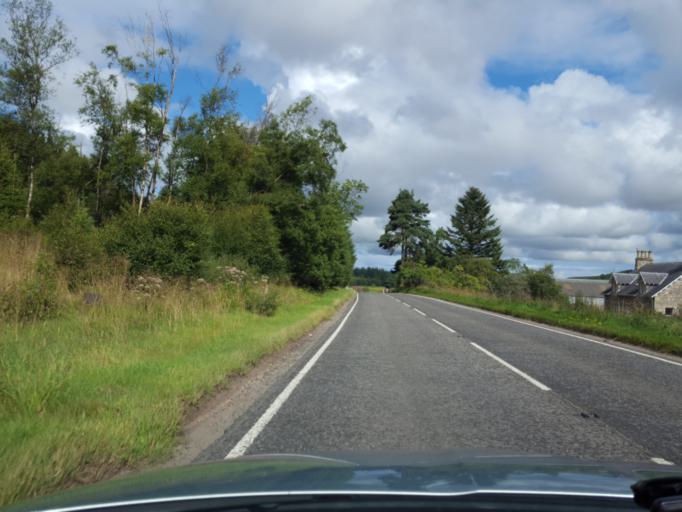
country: GB
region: Scotland
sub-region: Moray
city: Lhanbryd
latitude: 57.5694
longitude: -3.2583
